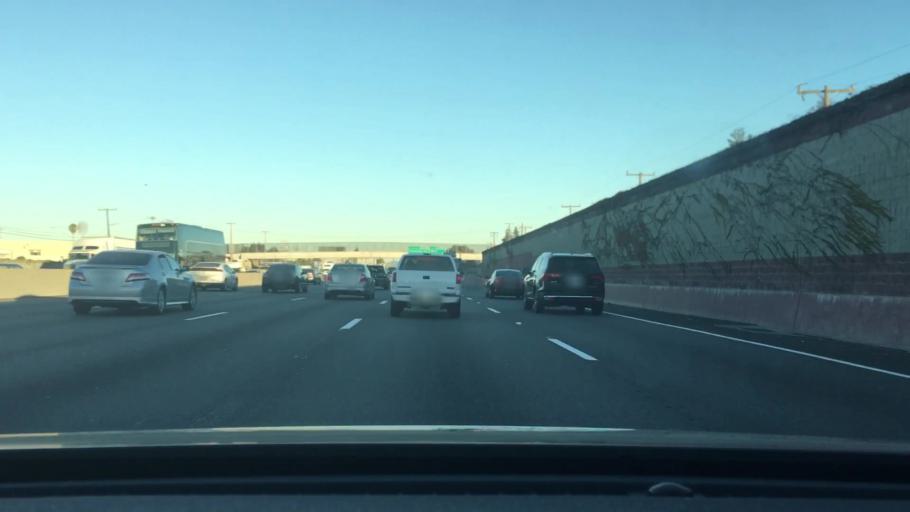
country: US
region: California
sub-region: San Mateo County
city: San Mateo
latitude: 37.5751
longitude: -122.3175
